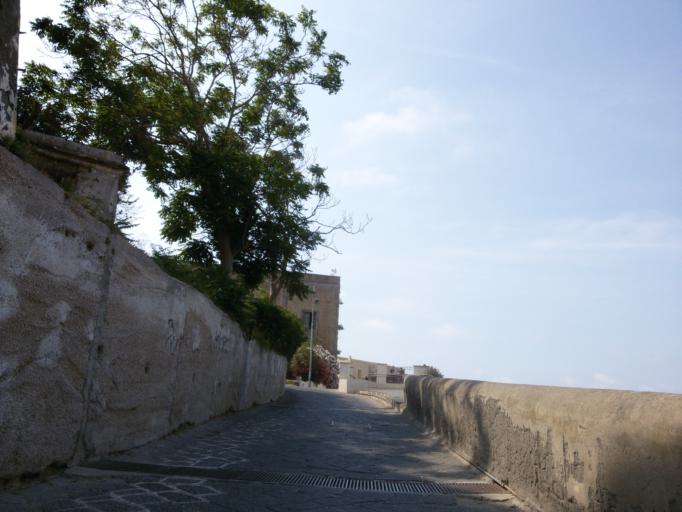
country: IT
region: Campania
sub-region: Provincia di Napoli
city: Procida
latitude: 40.7609
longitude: 14.0325
